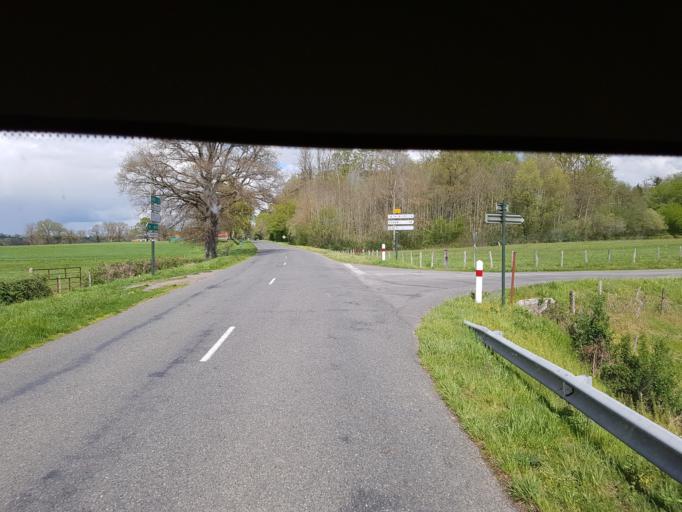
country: FR
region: Bourgogne
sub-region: Departement de Saone-et-Loire
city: Etang-sur-Arroux
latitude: 46.8064
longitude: 4.1556
